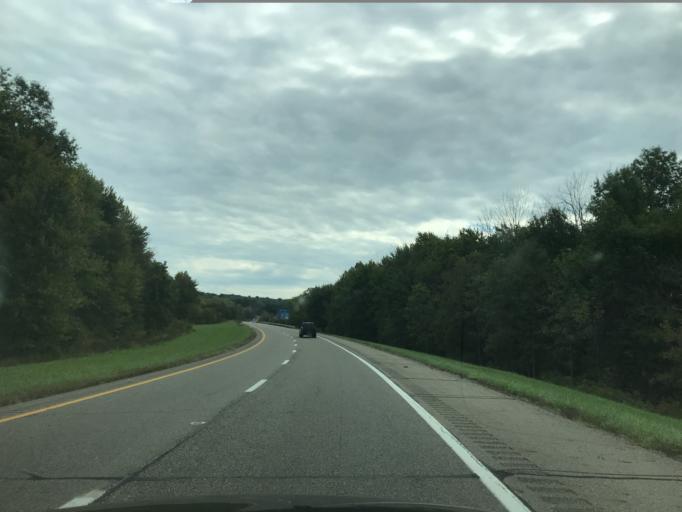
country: US
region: Ohio
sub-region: Trumbull County
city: Howland Center
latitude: 41.2350
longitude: -80.7582
